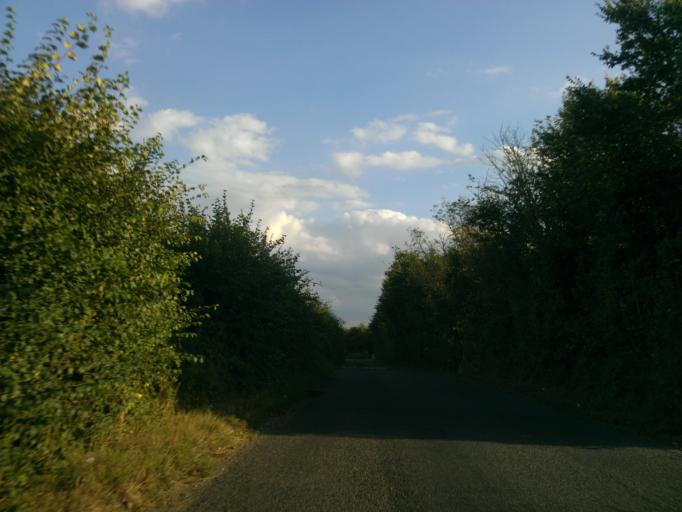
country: GB
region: England
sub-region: Essex
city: Rayne
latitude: 51.8522
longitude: 0.6034
